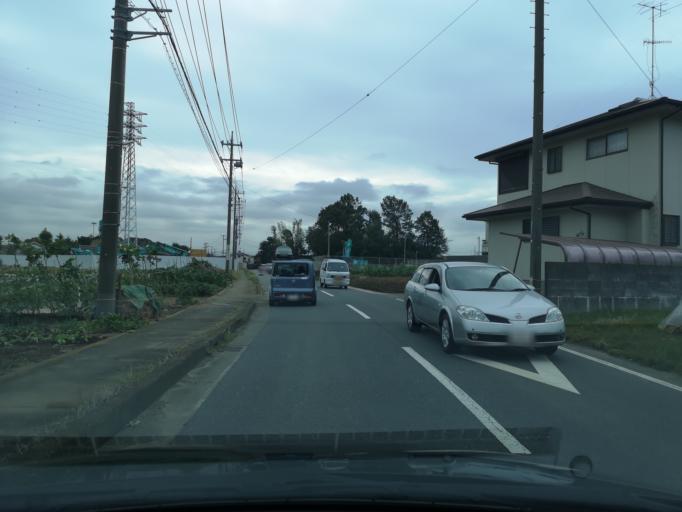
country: JP
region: Kanagawa
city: Atsugi
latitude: 35.3870
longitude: 139.3931
